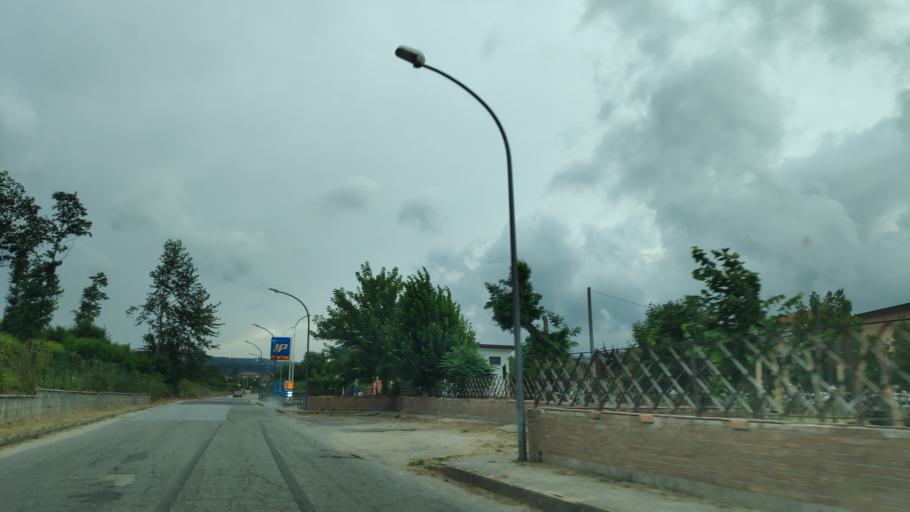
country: IT
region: Calabria
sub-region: Provincia di Vibo-Valentia
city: Serra San Bruno
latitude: 38.5727
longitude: 16.3304
